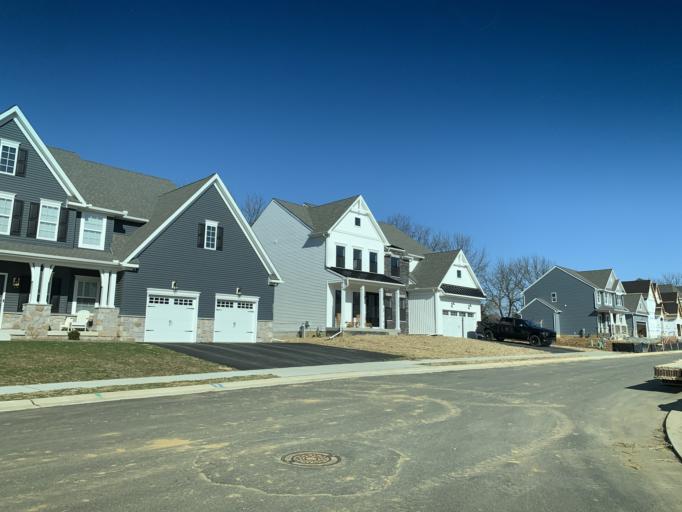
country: US
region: Maryland
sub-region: Harford County
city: South Bel Air
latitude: 39.5542
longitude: -76.3190
